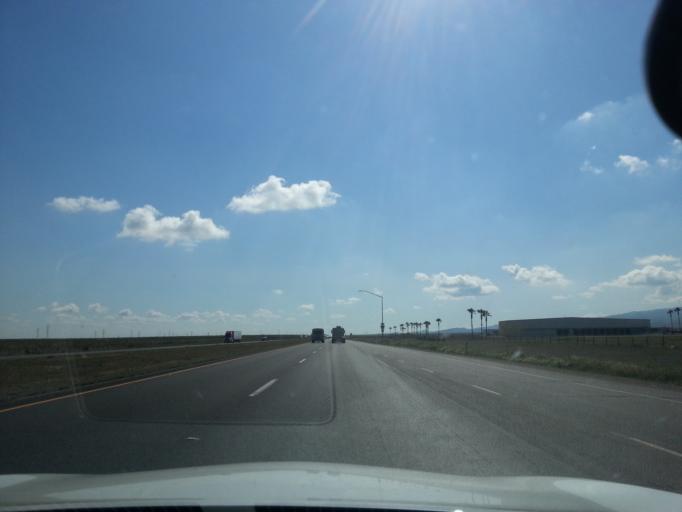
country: US
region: California
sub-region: Fresno County
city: San Joaquin
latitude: 36.4335
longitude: -120.3924
